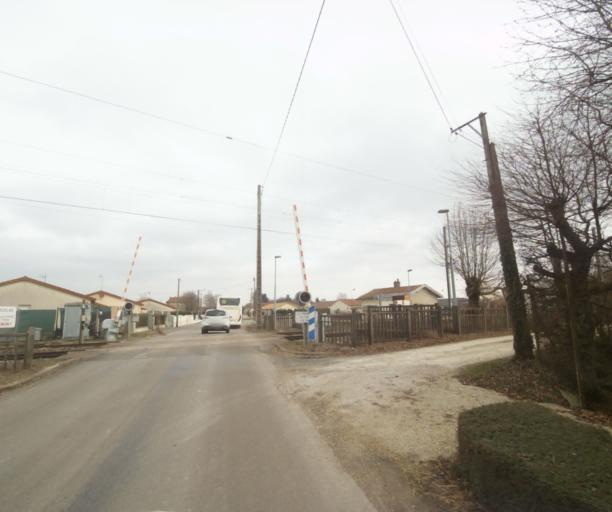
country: FR
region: Champagne-Ardenne
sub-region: Departement de la Haute-Marne
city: Villiers-en-Lieu
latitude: 48.6784
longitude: 4.8674
